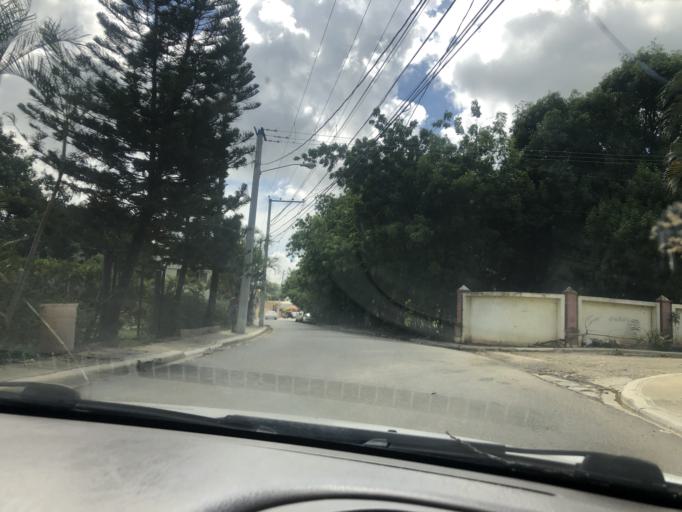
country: DO
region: Santiago
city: Santiago de los Caballeros
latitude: 19.4107
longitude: -70.7086
